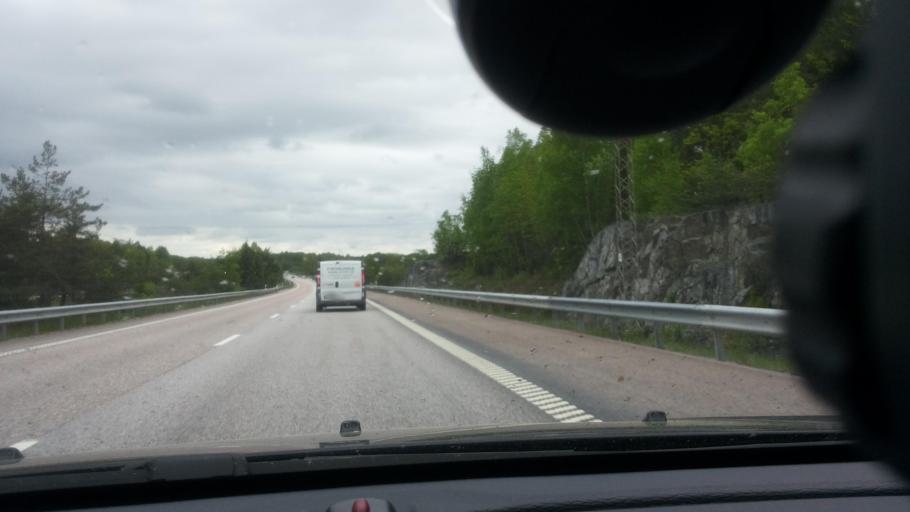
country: SE
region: Stockholm
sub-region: Sigtuna Kommun
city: Marsta
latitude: 59.6293
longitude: 17.9006
